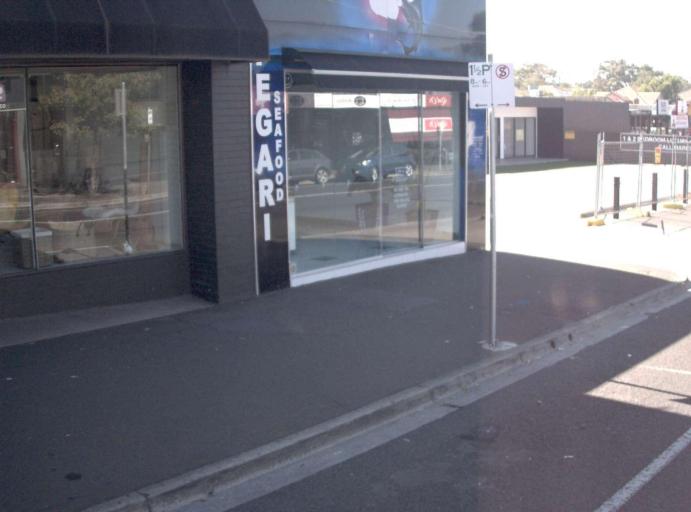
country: AU
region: Victoria
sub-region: Bayside
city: Hampton
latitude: -37.9353
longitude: 145.0029
